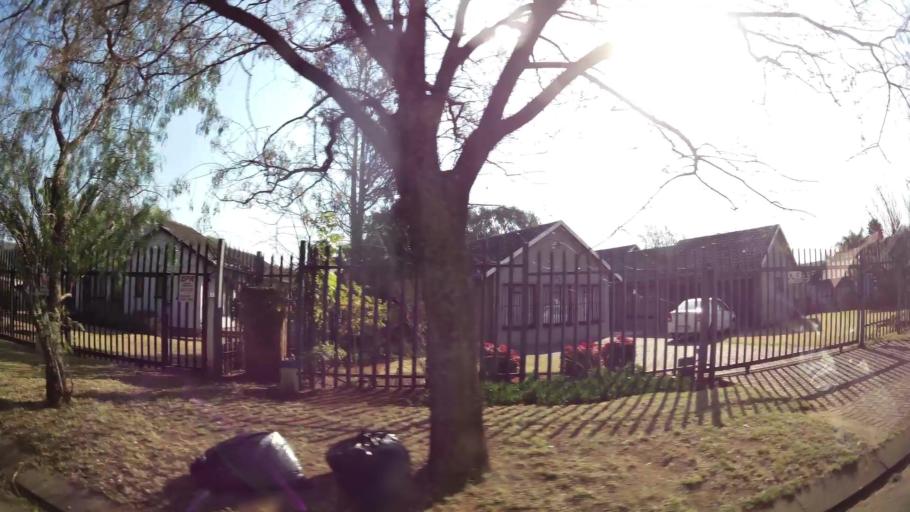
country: ZA
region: Gauteng
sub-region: West Rand District Municipality
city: Randfontein
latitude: -26.1750
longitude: 27.6898
